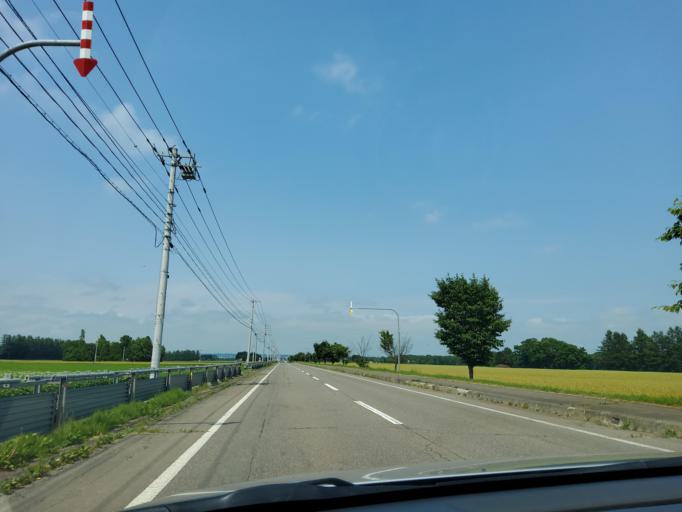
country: JP
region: Hokkaido
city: Obihiro
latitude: 42.8814
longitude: 143.0323
